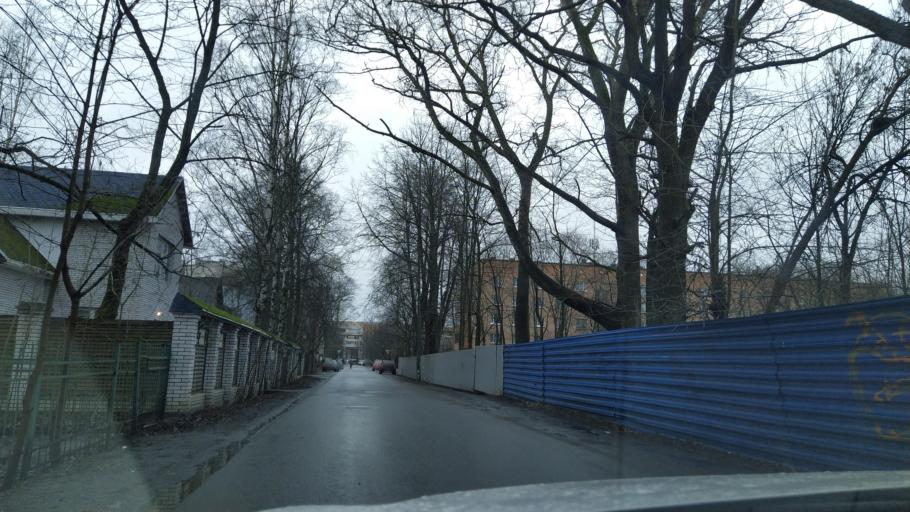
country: RU
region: St.-Petersburg
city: Pushkin
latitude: 59.7266
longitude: 30.4098
